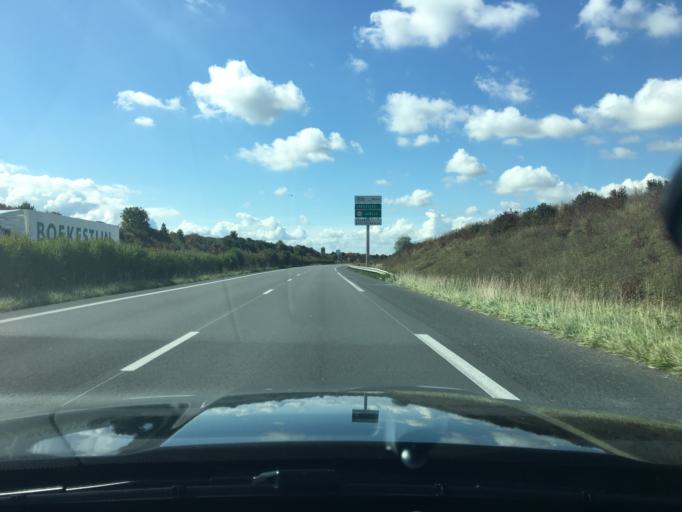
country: FR
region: Ile-de-France
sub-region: Departement du Val-d'Oise
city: Louvres
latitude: 49.0275
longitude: 2.5176
